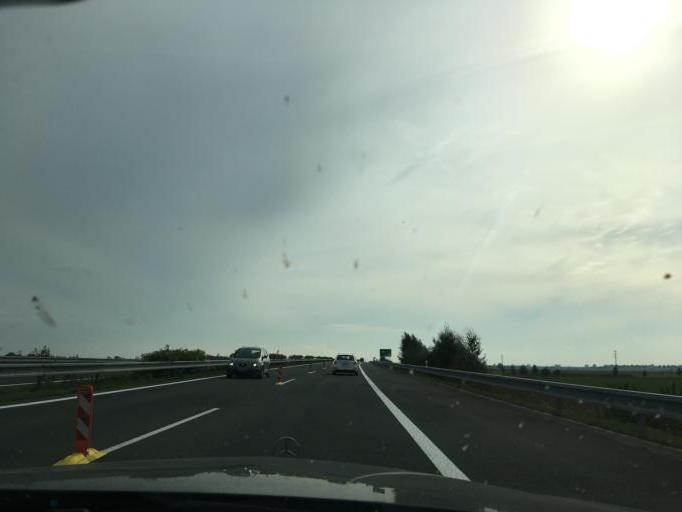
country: CZ
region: Pardubicky
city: Opatovice nad Labem
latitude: 50.1710
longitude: 15.7607
